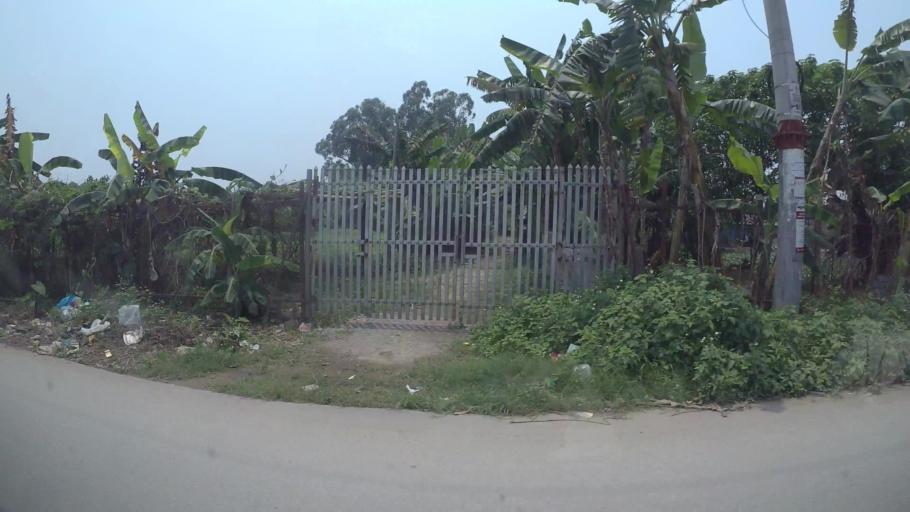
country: VN
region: Ha Noi
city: Ha Dong
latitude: 20.9982
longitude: 105.7650
